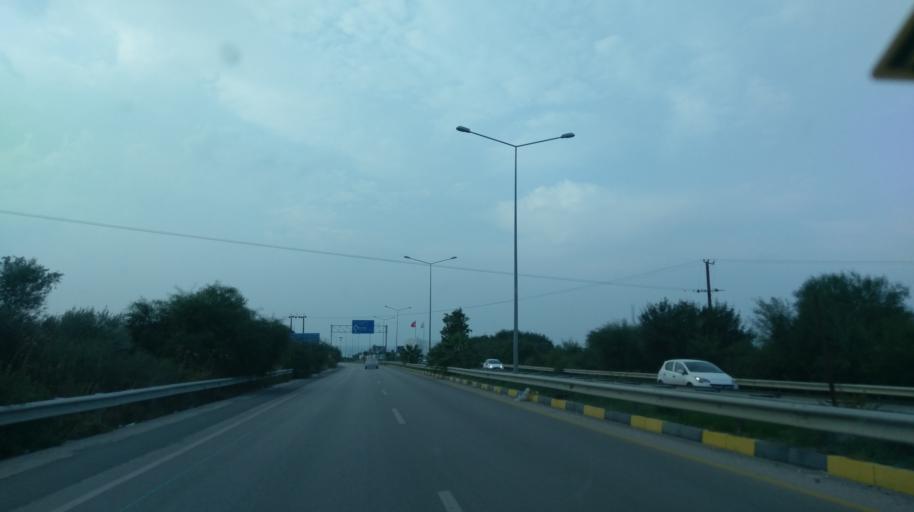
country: CY
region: Keryneia
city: Kyrenia
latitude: 35.3407
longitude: 33.2506
